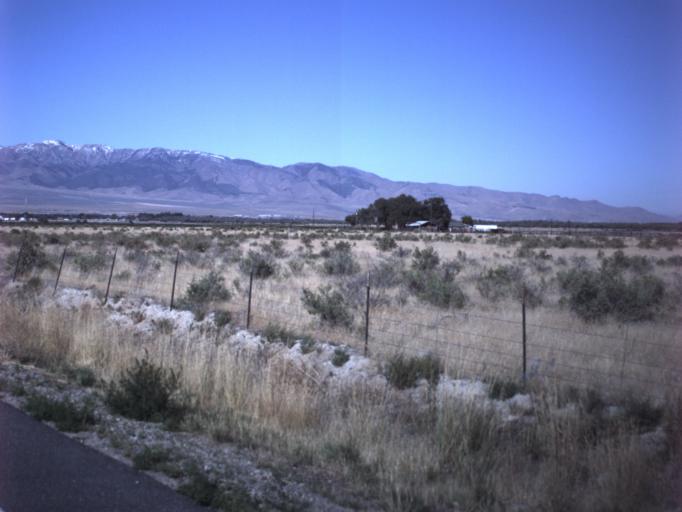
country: US
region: Utah
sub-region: Tooele County
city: Grantsville
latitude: 40.6016
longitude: -112.4040
